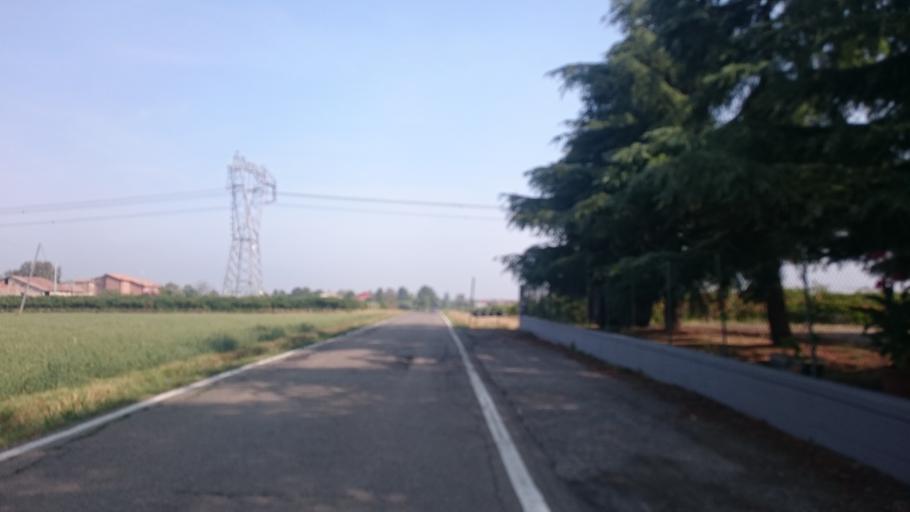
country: IT
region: Emilia-Romagna
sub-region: Provincia di Reggio Emilia
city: Albinea
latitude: 44.6377
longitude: 10.6249
